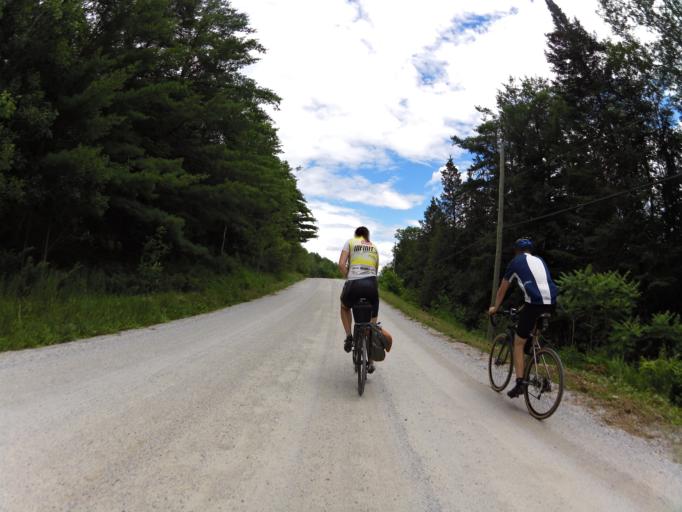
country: CA
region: Ontario
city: Renfrew
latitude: 45.1355
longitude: -76.6630
